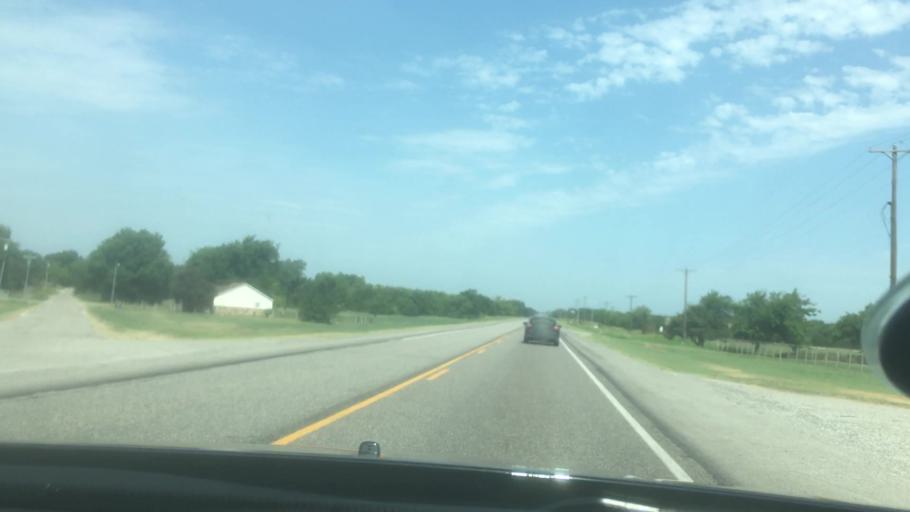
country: US
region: Oklahoma
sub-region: Seminole County
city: Konawa
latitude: 34.8689
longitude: -96.8383
